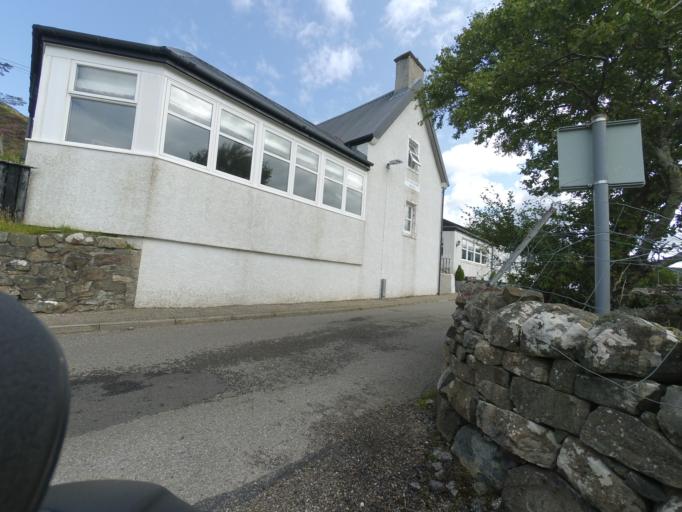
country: GB
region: Scotland
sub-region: Highland
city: Ullapool
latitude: 58.2433
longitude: -5.2022
